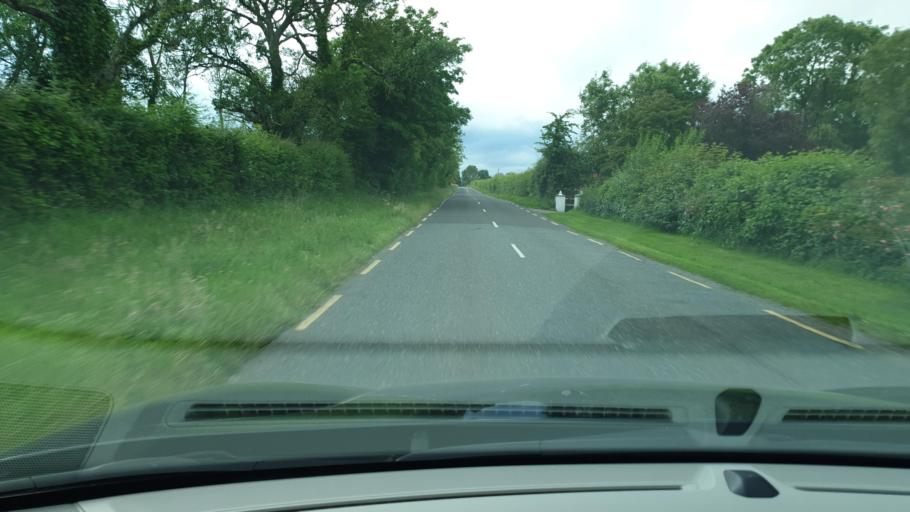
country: IE
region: Leinster
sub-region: An Mhi
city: Dunshaughlin
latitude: 53.5396
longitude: -6.5036
